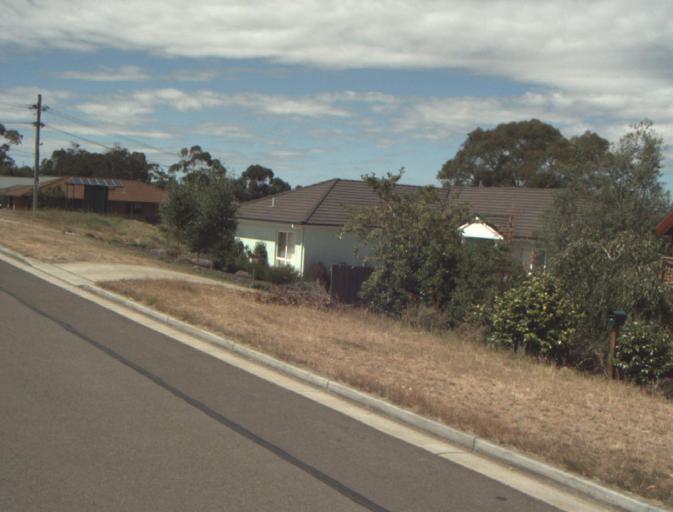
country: AU
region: Tasmania
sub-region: Launceston
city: West Launceston
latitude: -41.4550
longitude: 147.1227
